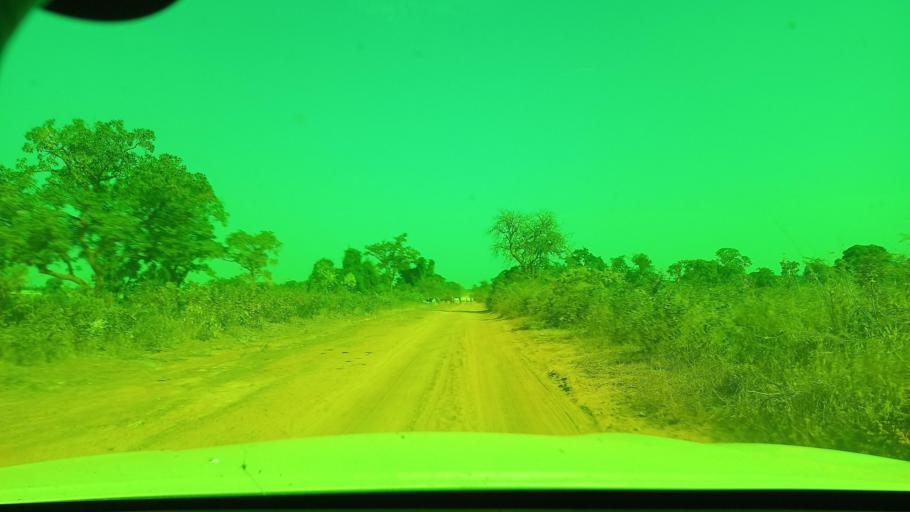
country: ML
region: Bamako
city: Bamako
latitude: 12.3974
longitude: -7.9930
